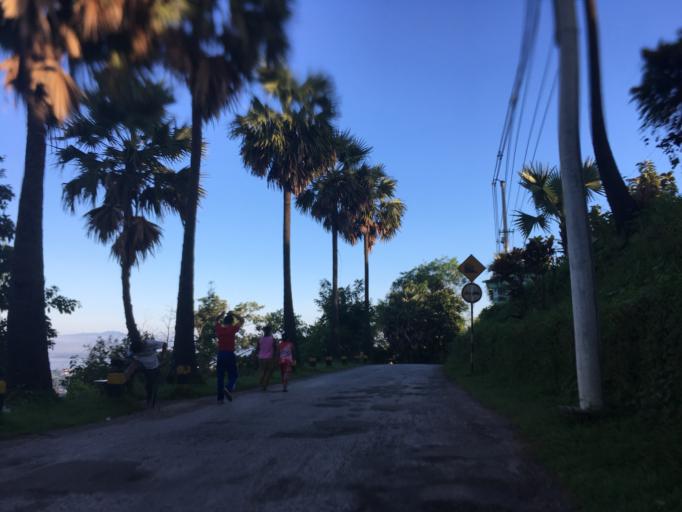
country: MM
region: Mon
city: Mawlamyine
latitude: 16.4814
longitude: 97.6284
